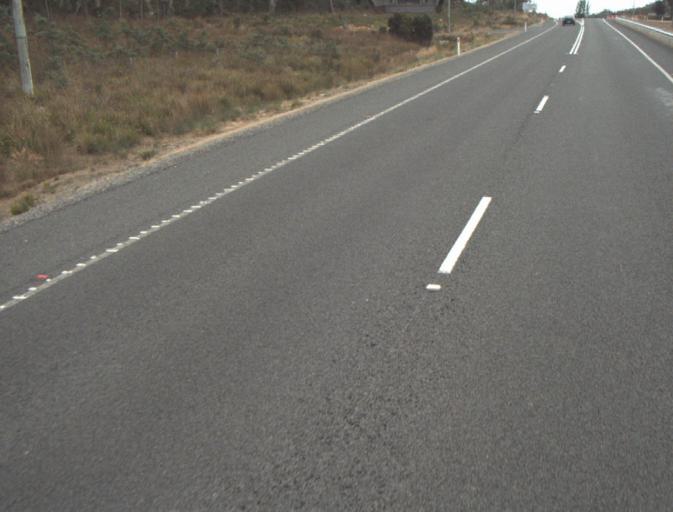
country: AU
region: Tasmania
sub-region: Launceston
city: Mayfield
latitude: -41.2696
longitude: 147.0345
